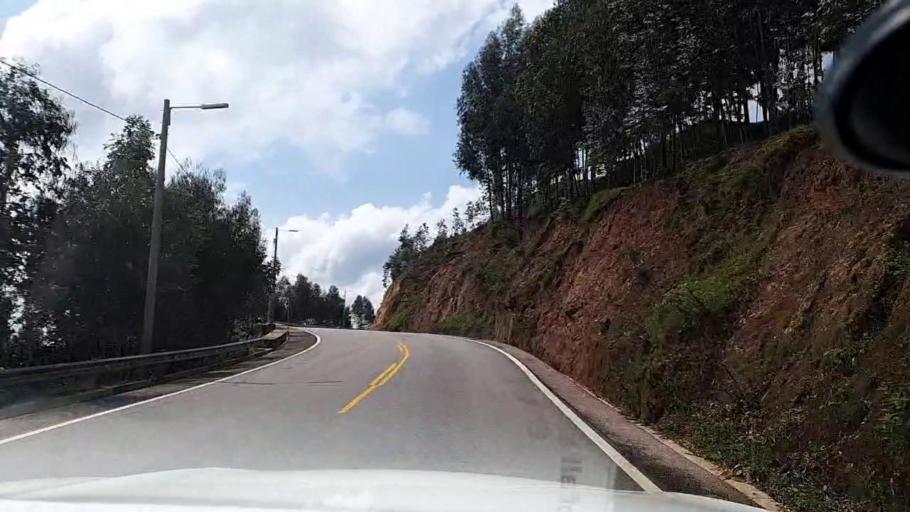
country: RW
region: Southern Province
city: Nzega
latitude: -2.5156
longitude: 29.4603
